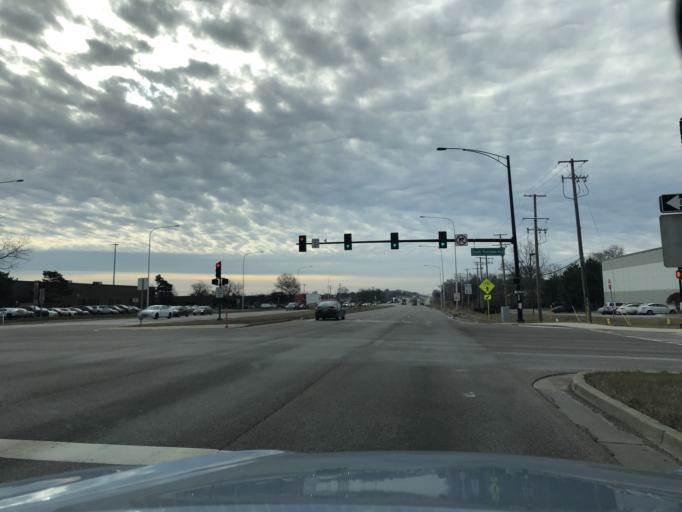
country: US
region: Illinois
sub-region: Cook County
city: Elk Grove Village
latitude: 41.9826
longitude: -87.9595
